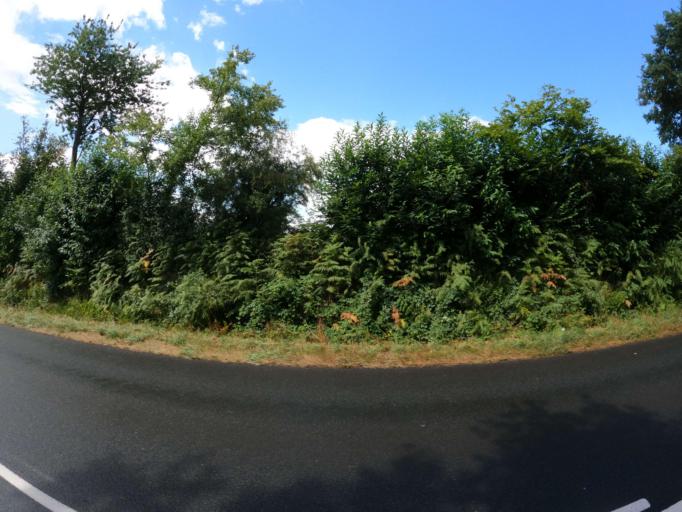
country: FR
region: Pays de la Loire
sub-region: Departement de Maine-et-Loire
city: Feneu
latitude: 47.6004
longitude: -0.5877
